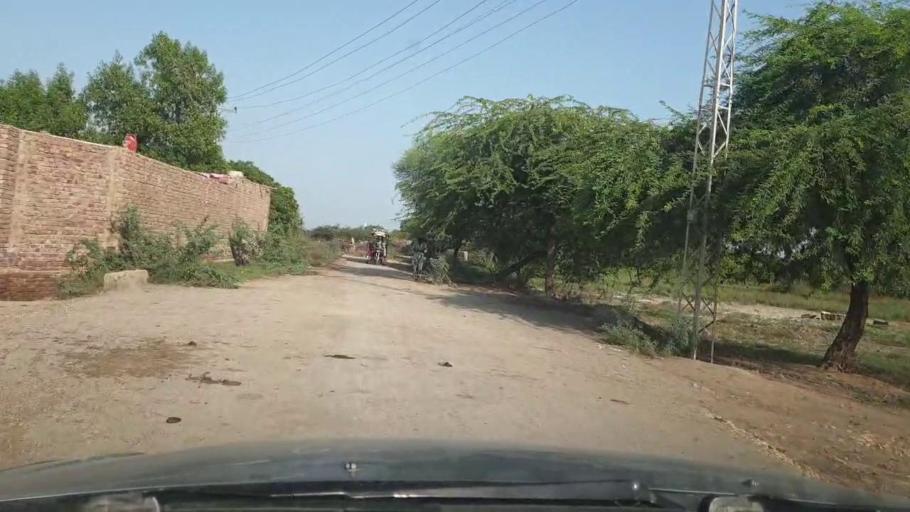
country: PK
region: Sindh
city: Tando Ghulam Ali
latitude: 25.2083
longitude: 68.9369
